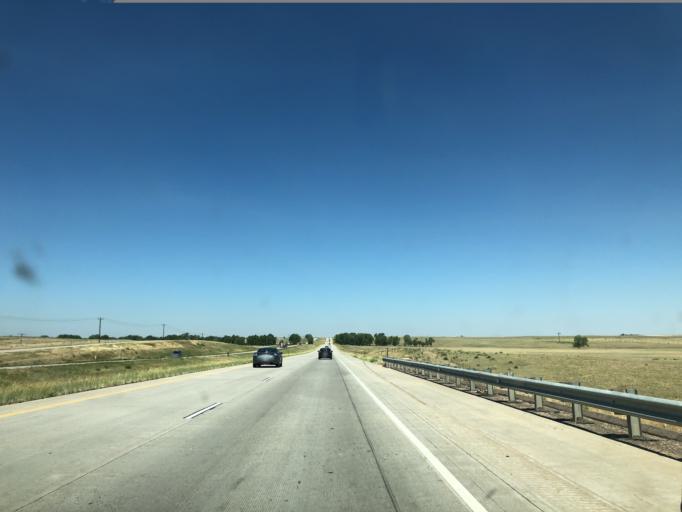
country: US
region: Colorado
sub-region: Arapahoe County
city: Byers
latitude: 39.6909
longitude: -104.1368
